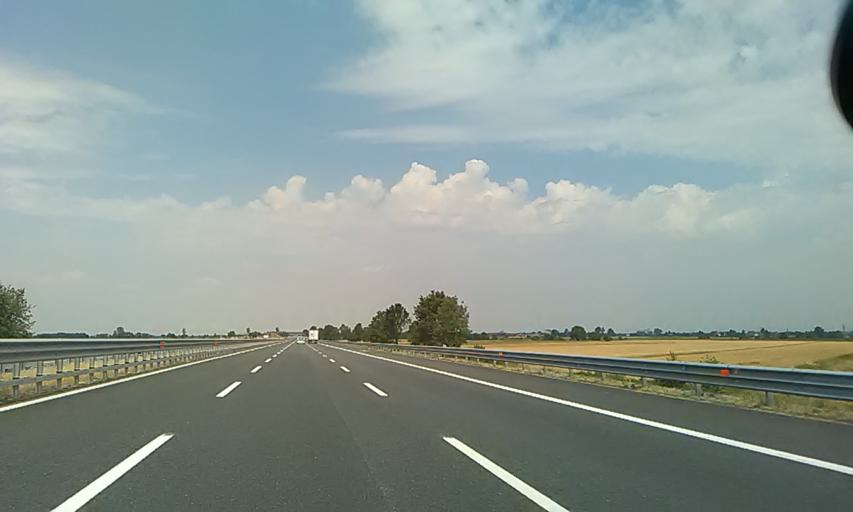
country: IT
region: Piedmont
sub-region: Provincia di Alessandria
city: Predosa
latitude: 44.7721
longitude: 8.6293
